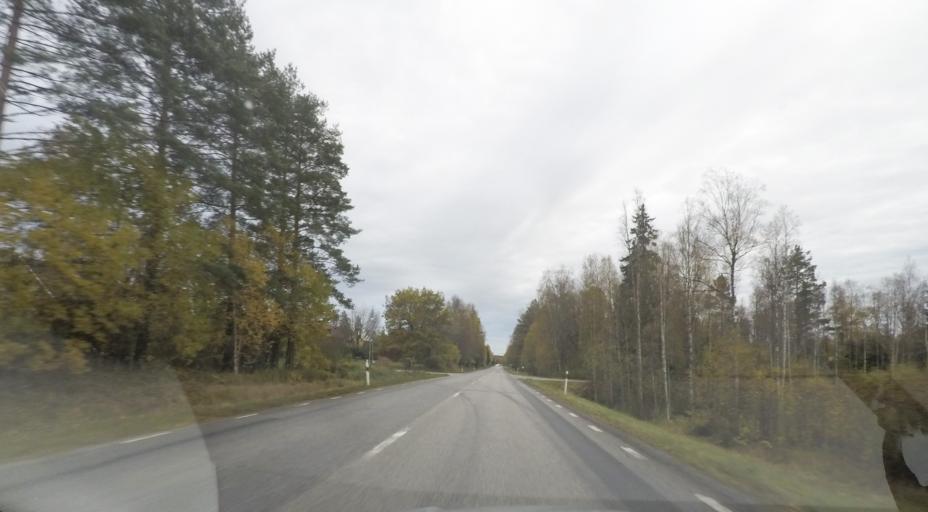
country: SE
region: OErebro
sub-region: Hallefors Kommun
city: Haellefors
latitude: 59.7463
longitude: 14.5115
